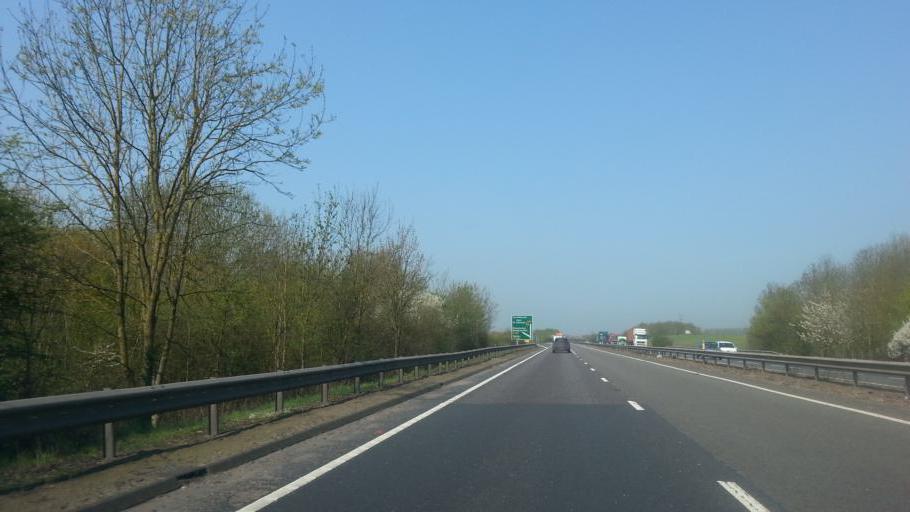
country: GB
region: England
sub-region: Suffolk
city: Needham Market
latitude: 52.1829
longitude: 1.0329
